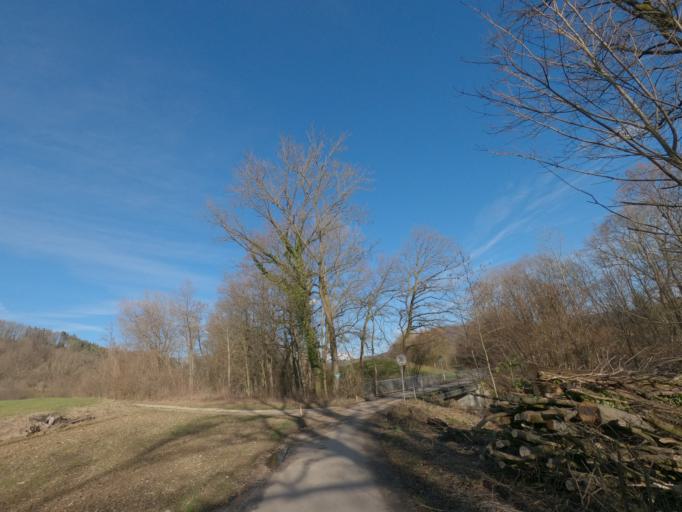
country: DE
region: Baden-Wuerttemberg
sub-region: Regierungsbezirk Stuttgart
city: Donzdorf
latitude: 48.6884
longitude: 9.7853
